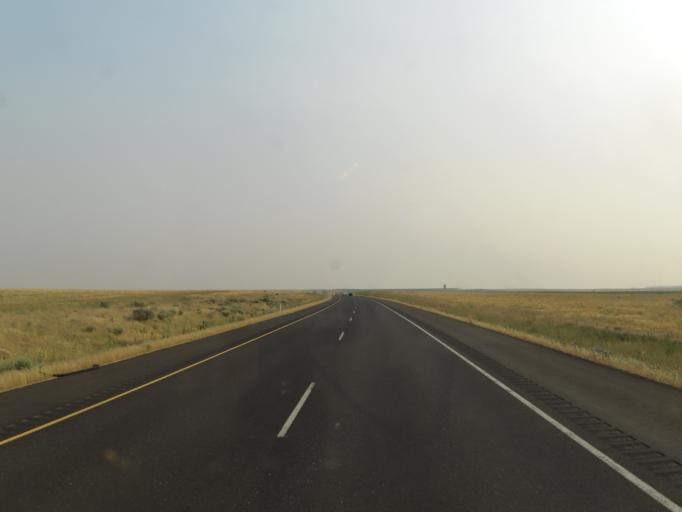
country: US
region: Washington
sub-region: Franklin County
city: Connell
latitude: 46.7164
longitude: -118.8361
